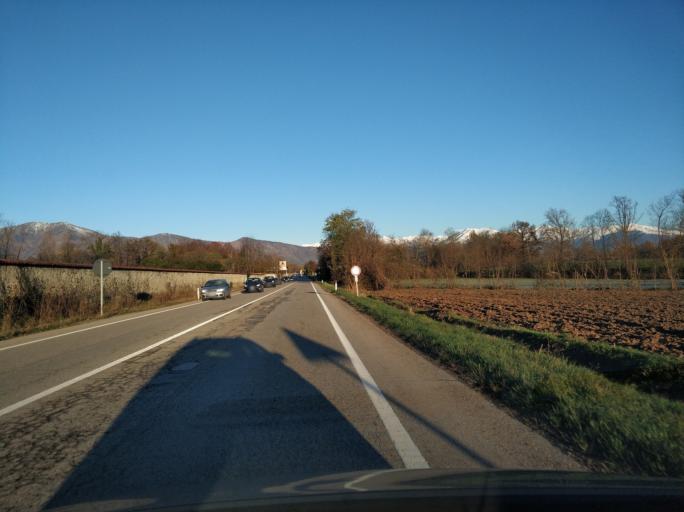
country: IT
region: Piedmont
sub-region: Provincia di Torino
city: Robassomero
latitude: 45.1823
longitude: 7.5759
